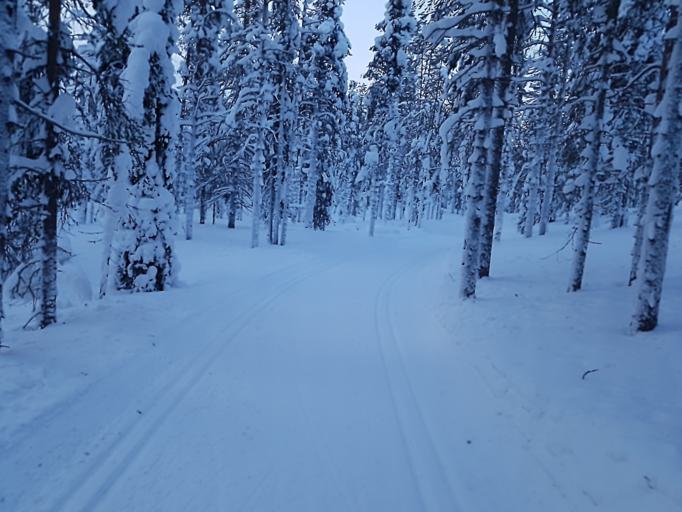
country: FI
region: Lapland
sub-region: Tunturi-Lappi
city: Kolari
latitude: 67.6456
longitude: 24.2349
